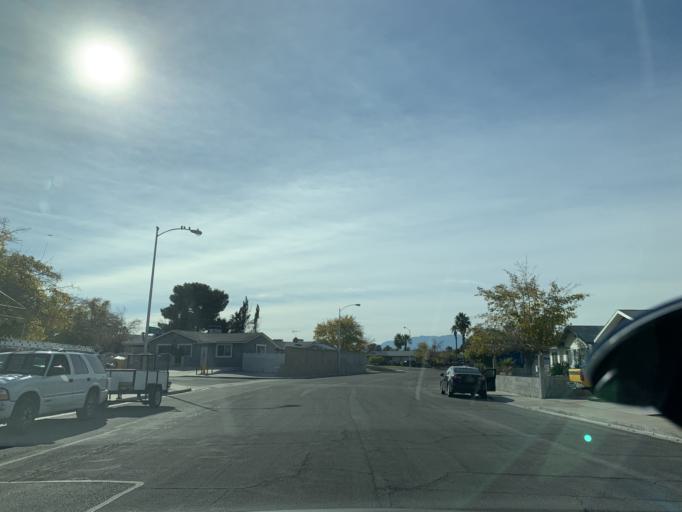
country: US
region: Nevada
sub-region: Clark County
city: Spring Valley
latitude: 36.1091
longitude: -115.2302
